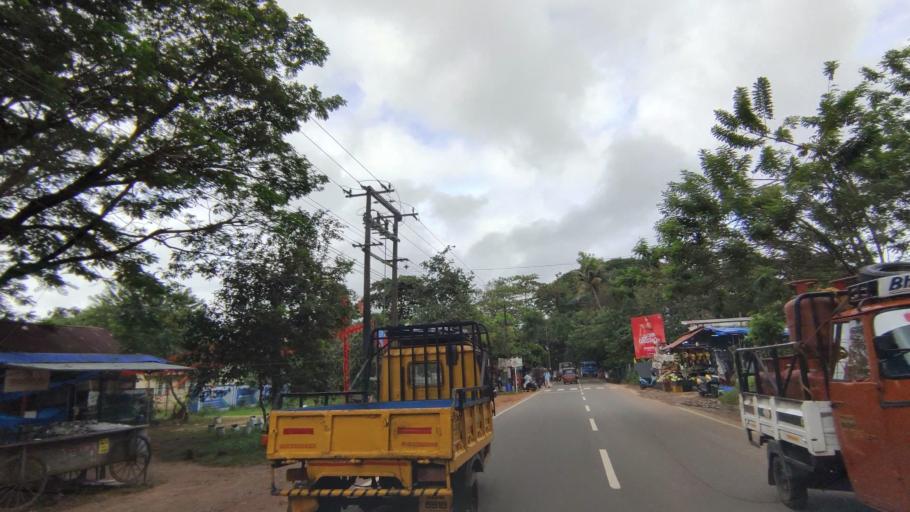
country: IN
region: Kerala
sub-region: Alappuzha
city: Shertallai
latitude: 9.6143
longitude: 76.3631
